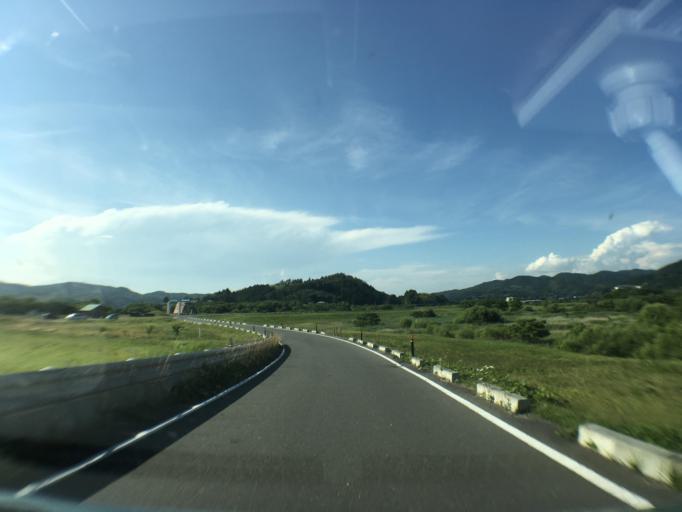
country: JP
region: Miyagi
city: Wakuya
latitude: 38.6023
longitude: 141.2924
